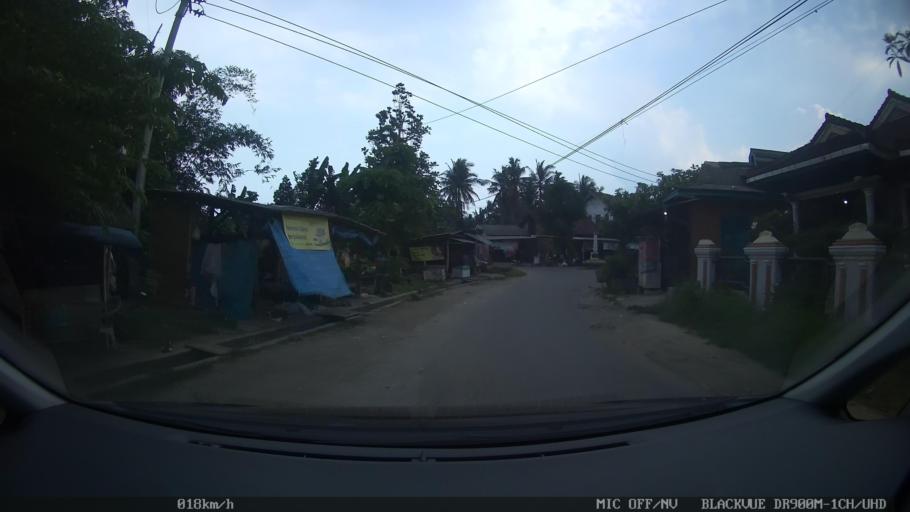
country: ID
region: Lampung
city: Kedaton
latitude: -5.3478
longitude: 105.2381
